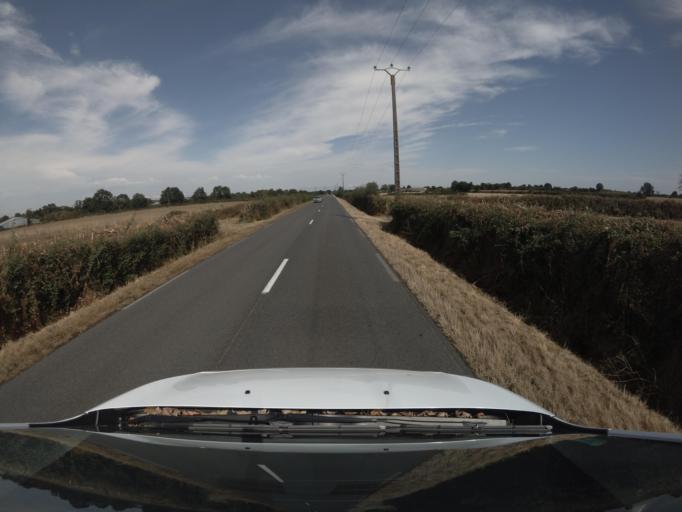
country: FR
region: Poitou-Charentes
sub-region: Departement des Deux-Sevres
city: Argenton-les-Vallees
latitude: 46.9816
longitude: -0.4896
